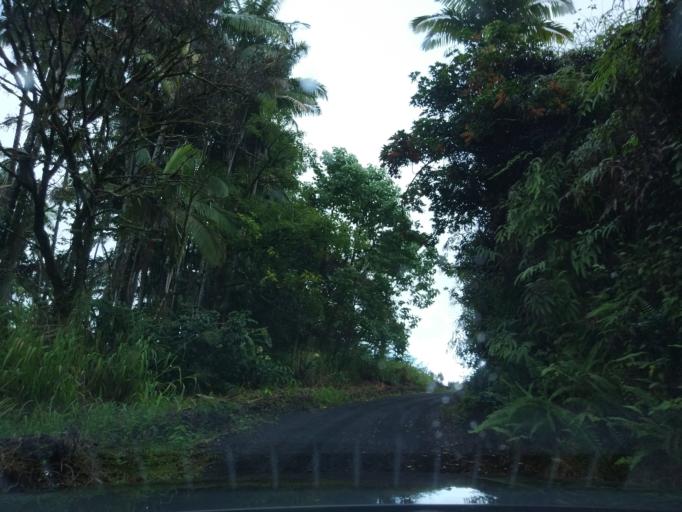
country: US
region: Hawaii
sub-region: Hawaii County
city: Pepeekeo
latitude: 19.8761
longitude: -155.1416
